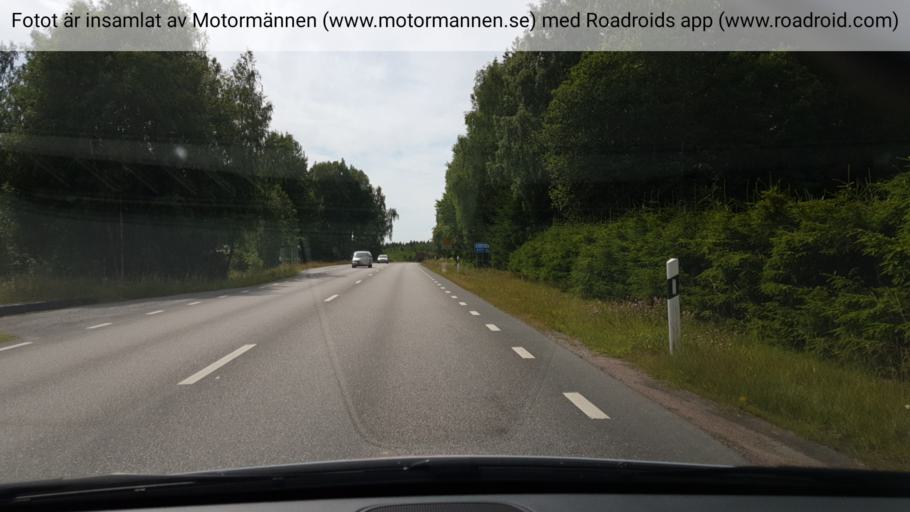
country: SE
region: Vaestra Goetaland
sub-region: Tibro Kommun
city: Tibro
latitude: 58.3421
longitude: 14.1742
